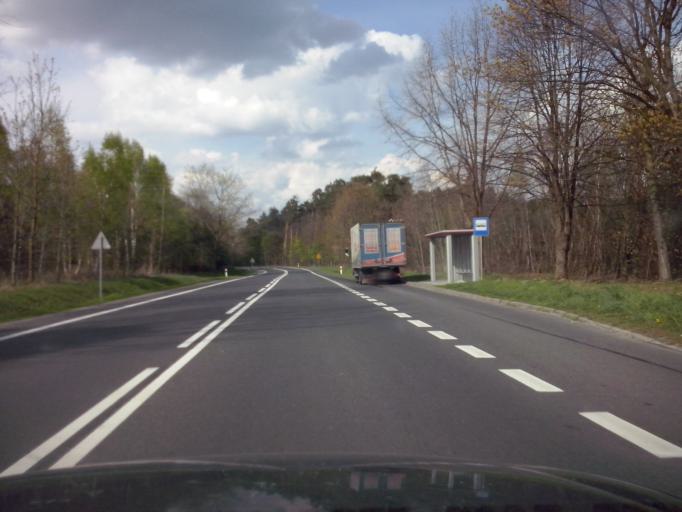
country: PL
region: Subcarpathian Voivodeship
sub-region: Powiat rzeszowski
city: Gorno
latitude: 50.2623
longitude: 22.1398
